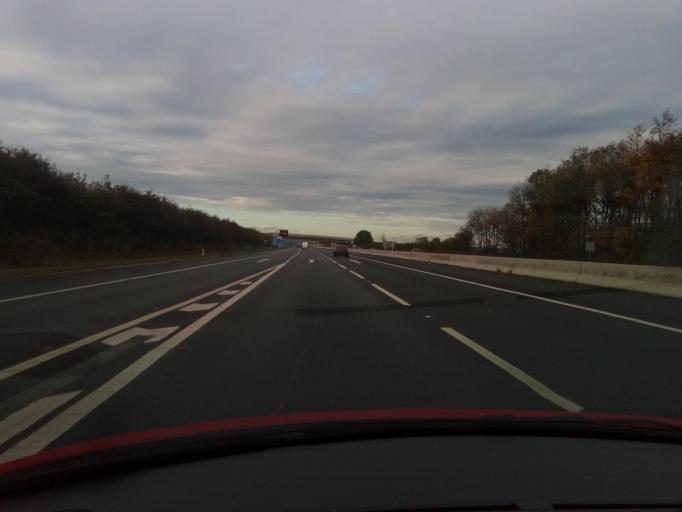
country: GB
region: England
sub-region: North Yorkshire
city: Catterick
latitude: 54.4482
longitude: -1.6685
